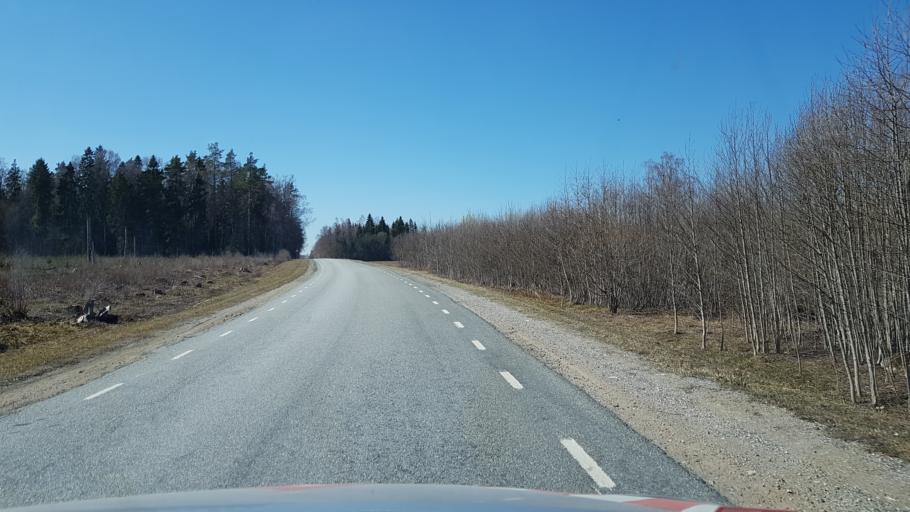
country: EE
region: Laeaene-Virumaa
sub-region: Vaeike-Maarja vald
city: Vaike-Maarja
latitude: 59.1233
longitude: 26.3078
